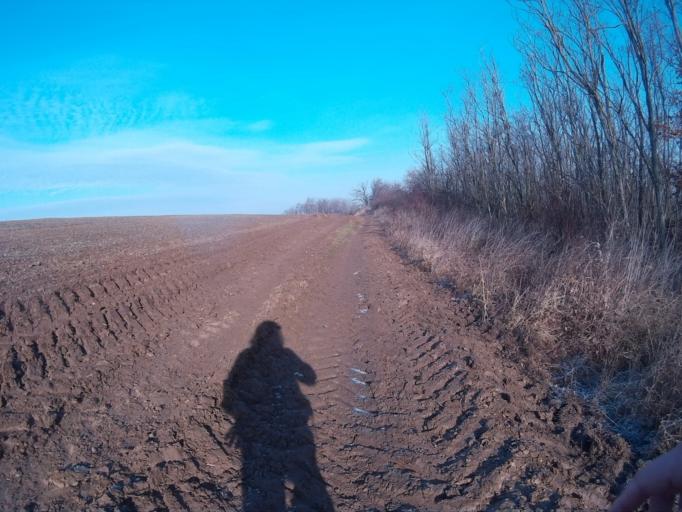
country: HU
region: Nograd
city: Bercel
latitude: 47.9375
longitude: 19.4279
